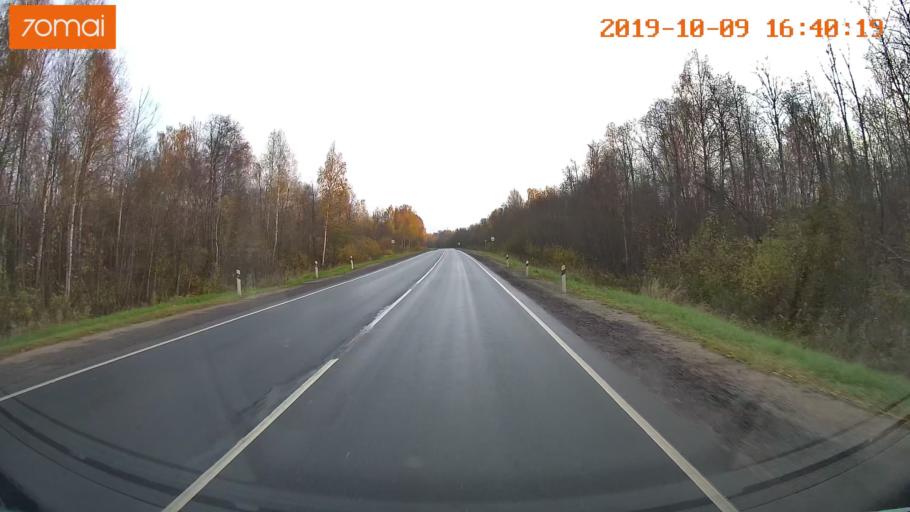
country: RU
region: Kostroma
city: Volgorechensk
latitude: 57.4853
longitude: 41.0591
